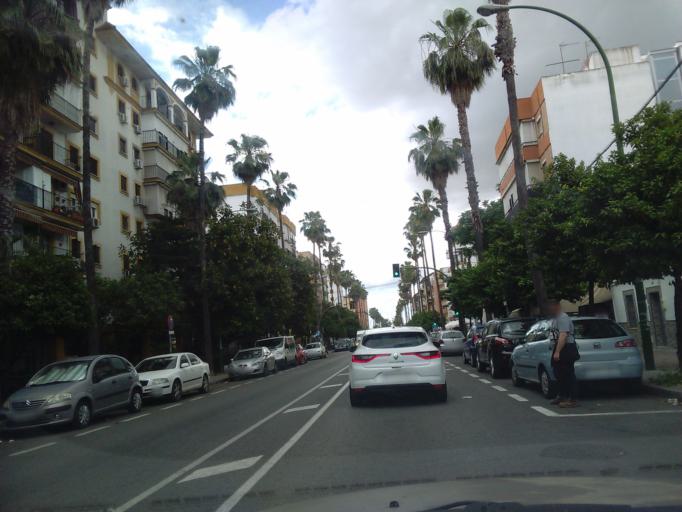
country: ES
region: Andalusia
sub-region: Provincia de Sevilla
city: Sevilla
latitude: 37.3696
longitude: -5.9526
